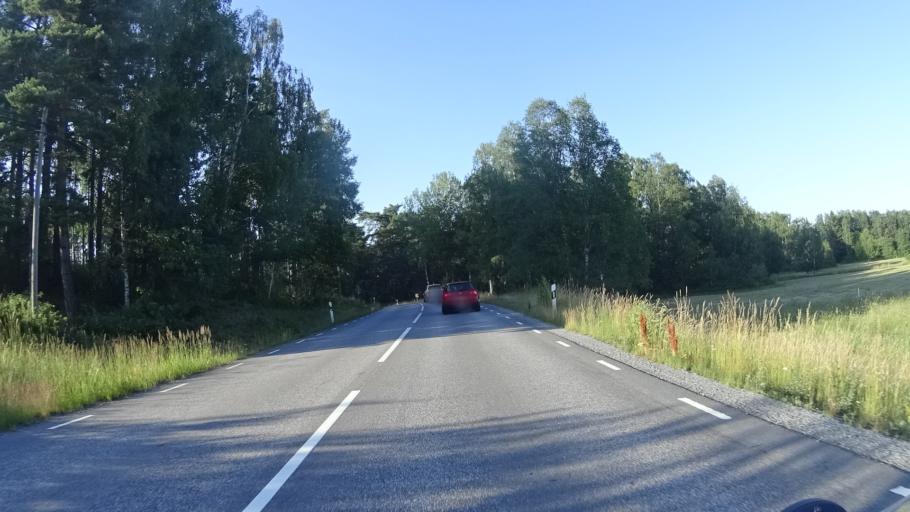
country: SE
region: Stockholm
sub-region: Sodertalje Kommun
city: Pershagen
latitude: 59.1045
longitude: 17.6348
